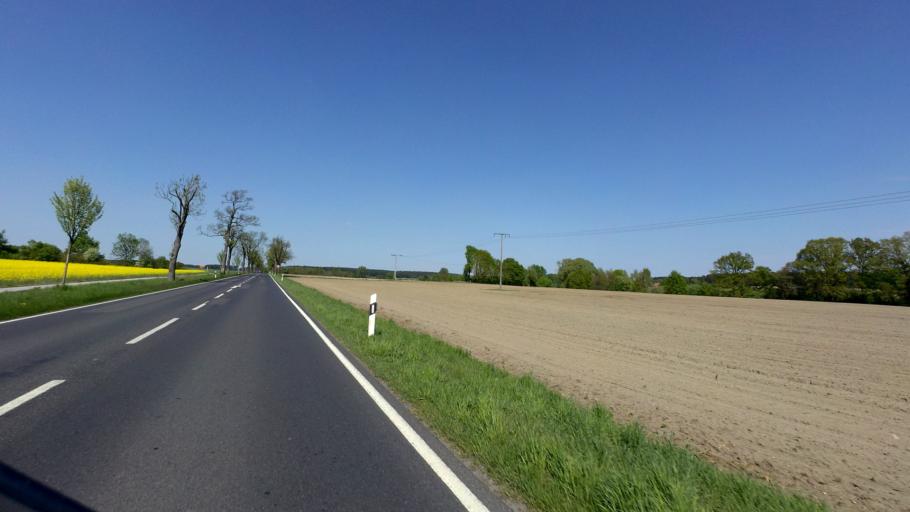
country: DE
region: Brandenburg
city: Friedland
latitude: 52.1250
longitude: 14.2568
